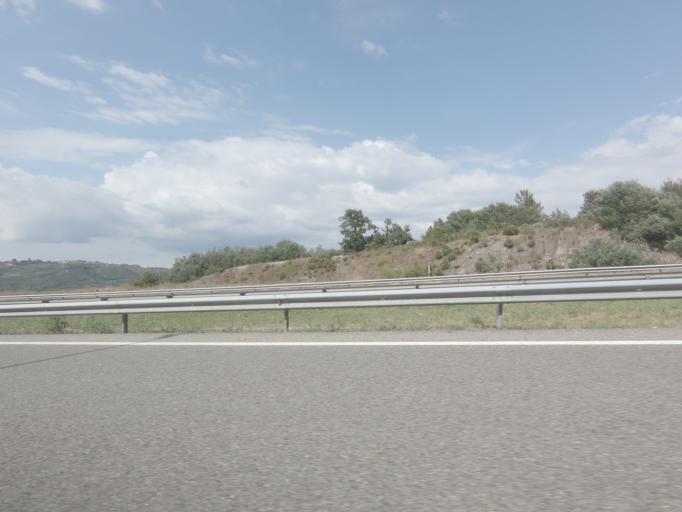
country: ES
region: Galicia
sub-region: Provincia de Ourense
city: Ourense
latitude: 42.3451
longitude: -7.8871
